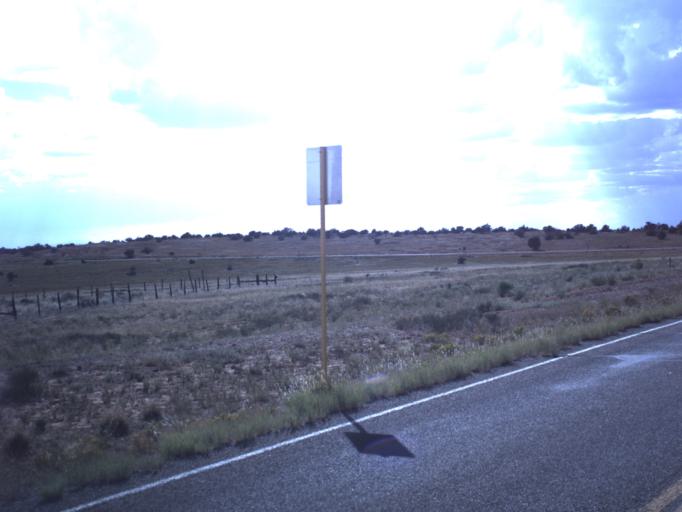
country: US
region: Utah
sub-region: Grand County
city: Moab
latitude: 38.5521
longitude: -109.7885
